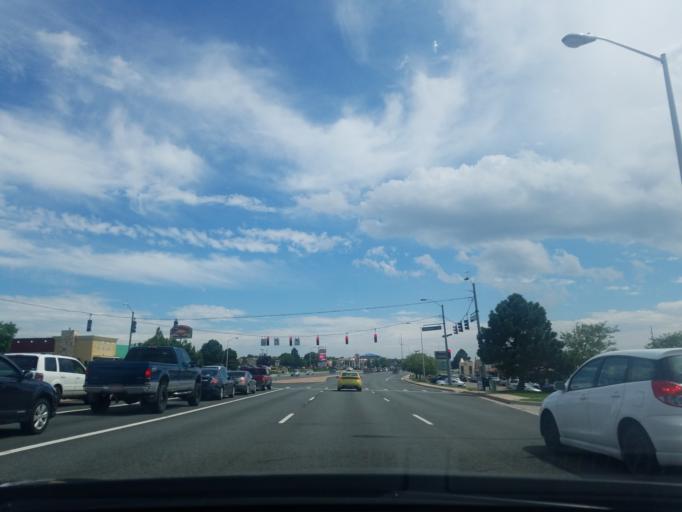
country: US
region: Colorado
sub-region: El Paso County
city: Air Force Academy
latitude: 38.9474
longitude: -104.8026
